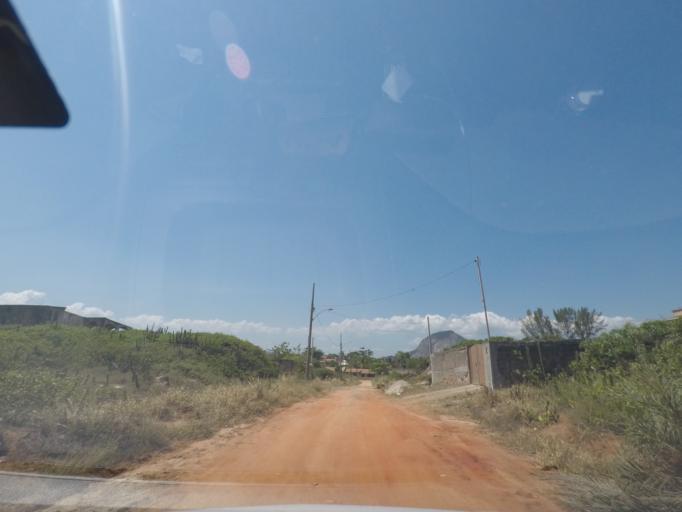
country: BR
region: Rio de Janeiro
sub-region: Marica
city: Marica
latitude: -22.9739
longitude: -42.9233
